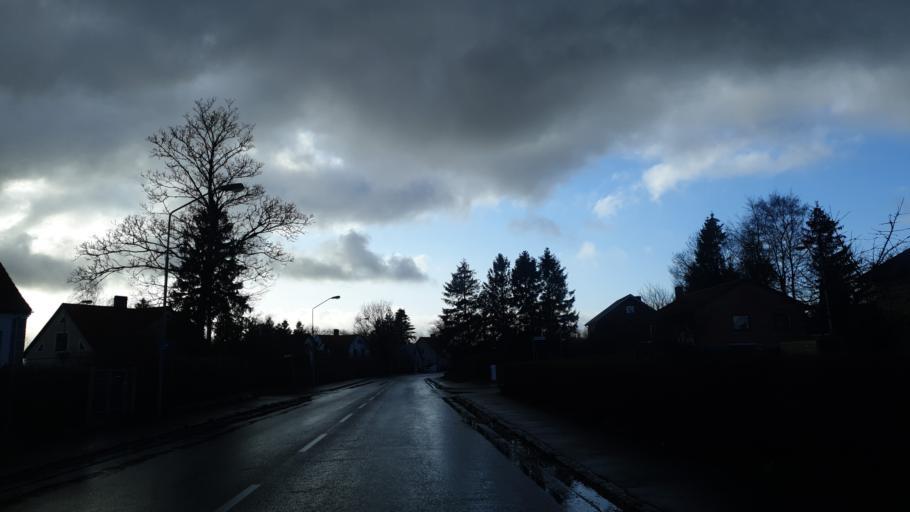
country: SE
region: Skane
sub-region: Skurups Kommun
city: Rydsgard
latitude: 55.4713
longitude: 13.5824
